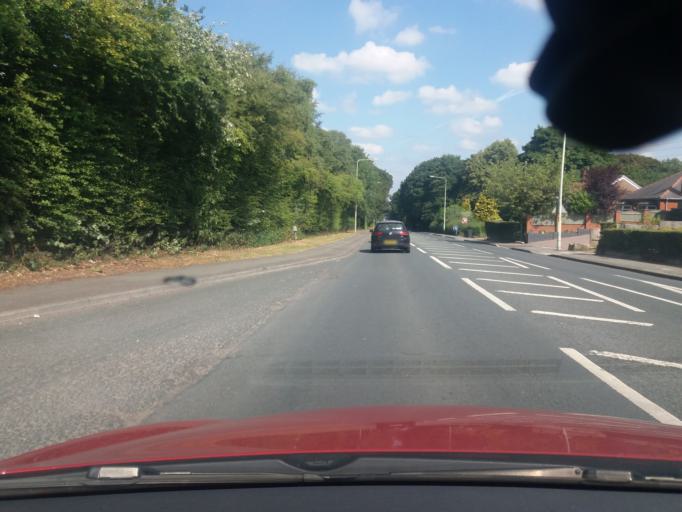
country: GB
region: England
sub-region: Lancashire
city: Chorley
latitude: 53.6345
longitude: -2.6142
